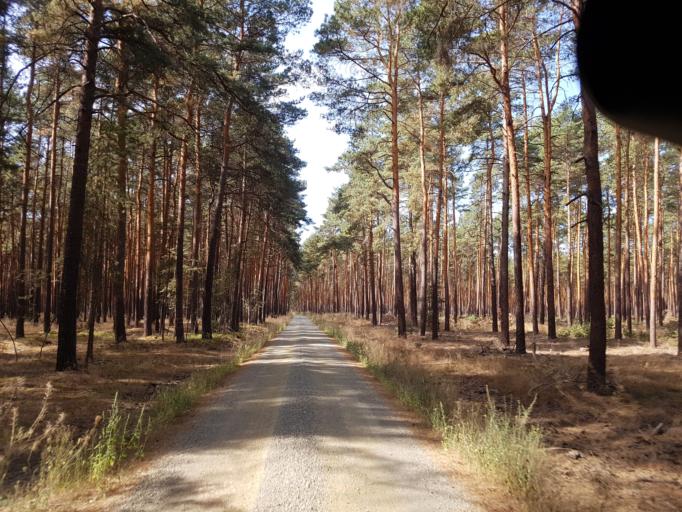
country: DE
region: Brandenburg
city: Sonnewalde
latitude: 51.7593
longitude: 13.6463
